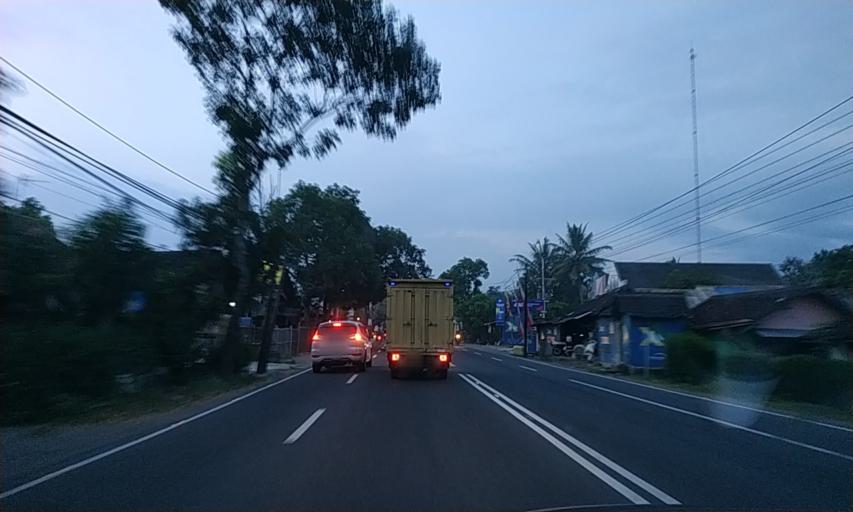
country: ID
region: Daerah Istimewa Yogyakarta
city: Godean
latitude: -7.8382
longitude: 110.2199
